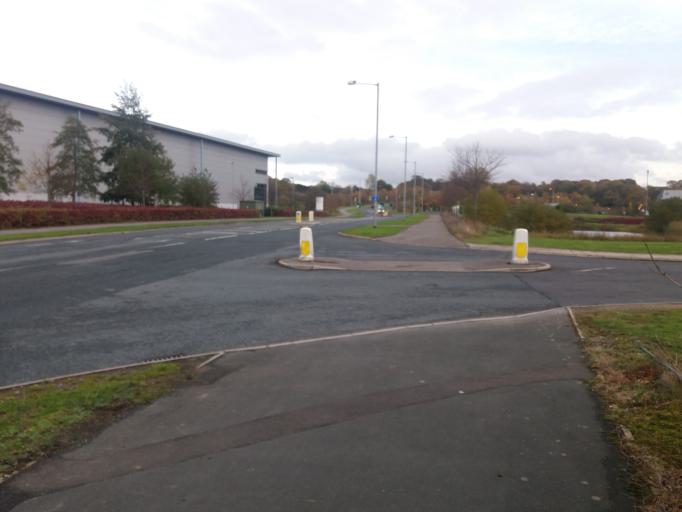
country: GB
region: England
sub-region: Lancashire
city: Euxton
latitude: 53.6732
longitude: -2.6438
